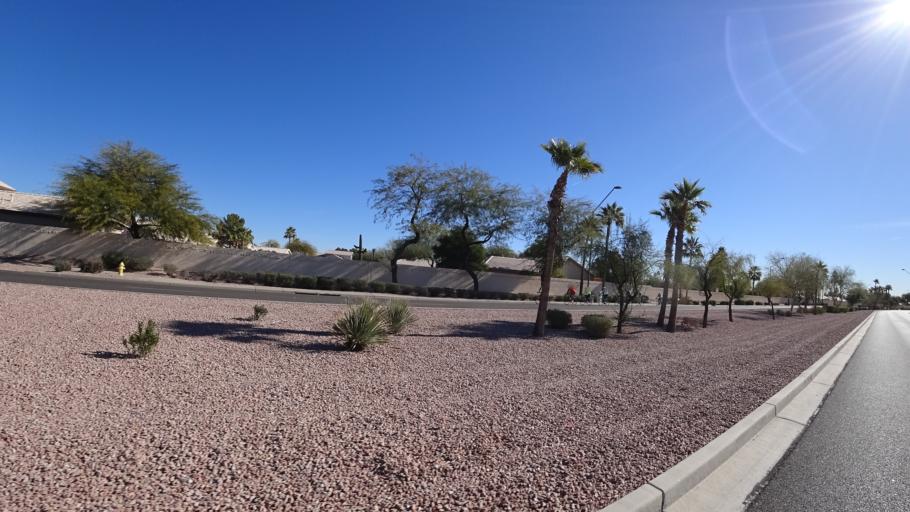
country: US
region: Arizona
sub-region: Maricopa County
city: Litchfield Park
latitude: 33.4849
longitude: -112.3953
